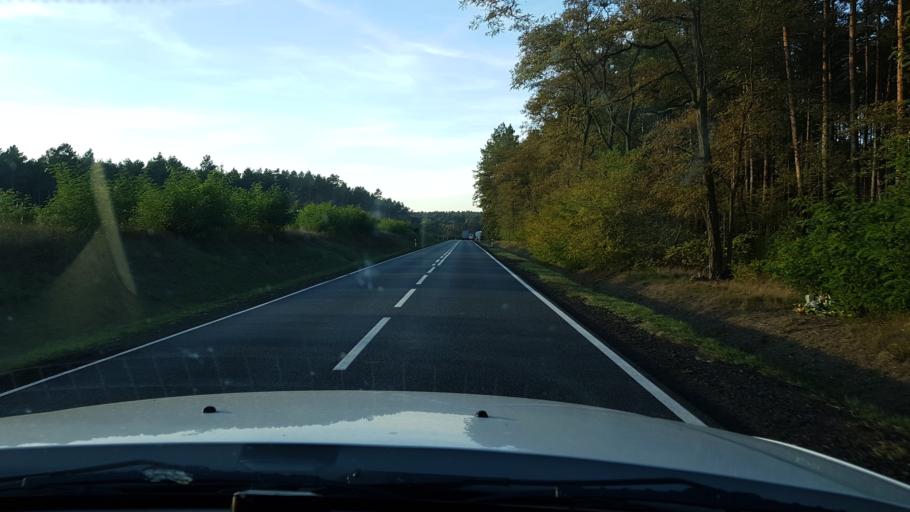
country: PL
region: West Pomeranian Voivodeship
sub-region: Powiat gryfinski
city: Chojna
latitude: 52.9697
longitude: 14.3843
